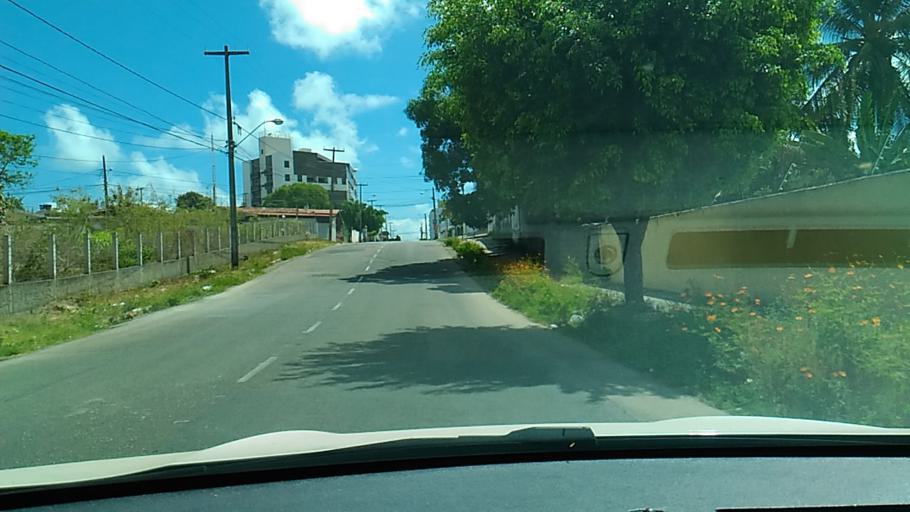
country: BR
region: Paraiba
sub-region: Joao Pessoa
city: Joao Pessoa
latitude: -7.1519
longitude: -34.8443
